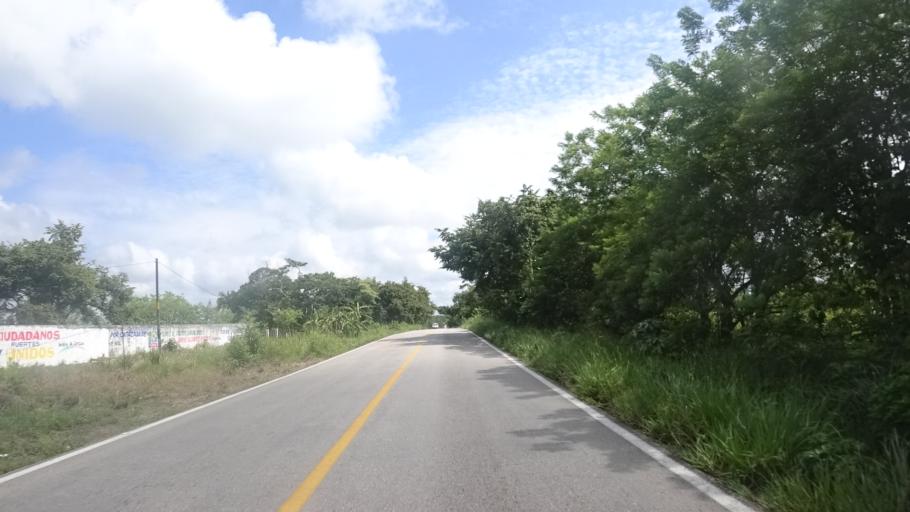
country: MX
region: Chiapas
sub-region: Catazaja
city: Catazaja
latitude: 17.6709
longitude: -92.0321
